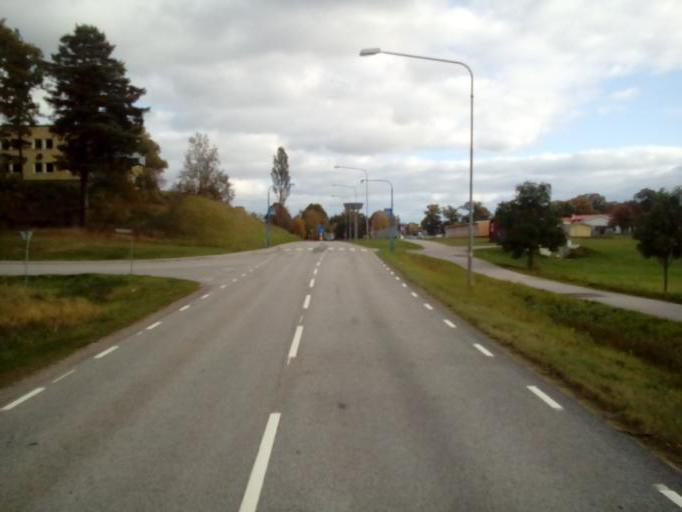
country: SE
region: Kalmar
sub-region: Vasterviks Kommun
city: Gamleby
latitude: 57.8932
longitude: 16.3953
